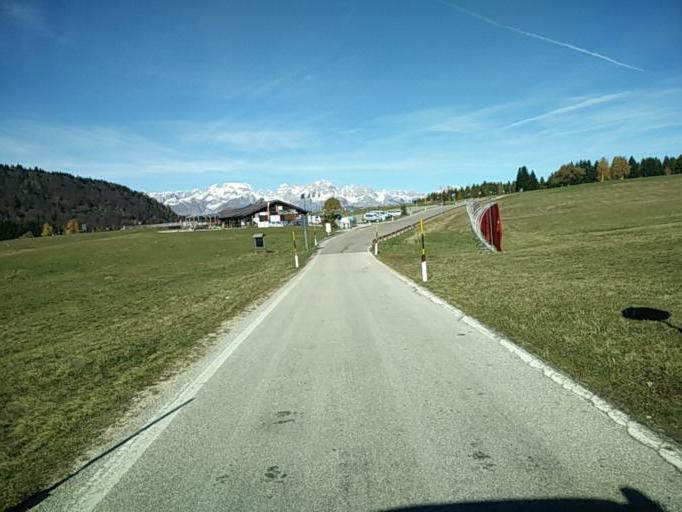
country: IT
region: Trentino-Alto Adige
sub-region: Provincia di Trento
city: Cimoneri
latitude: 46.0195
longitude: 11.0436
